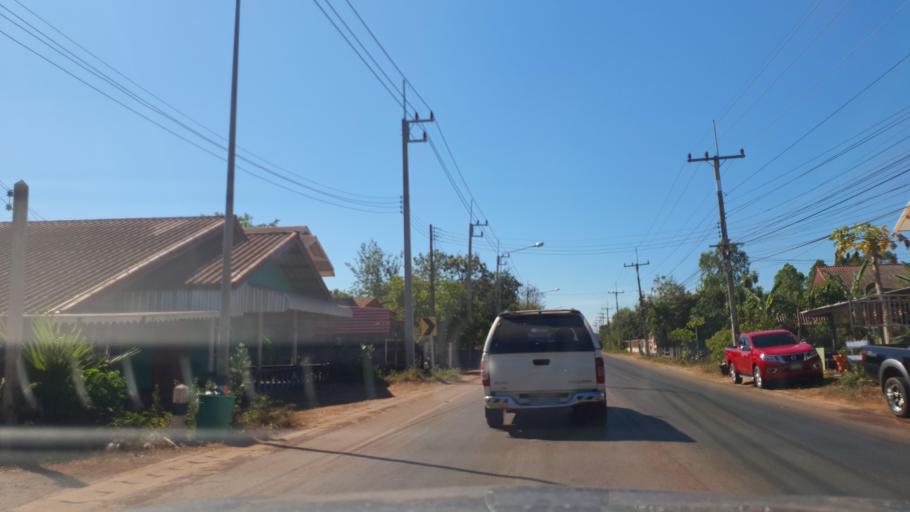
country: TH
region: Sakon Nakhon
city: Phon Na Kaeo
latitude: 17.2637
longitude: 104.1914
